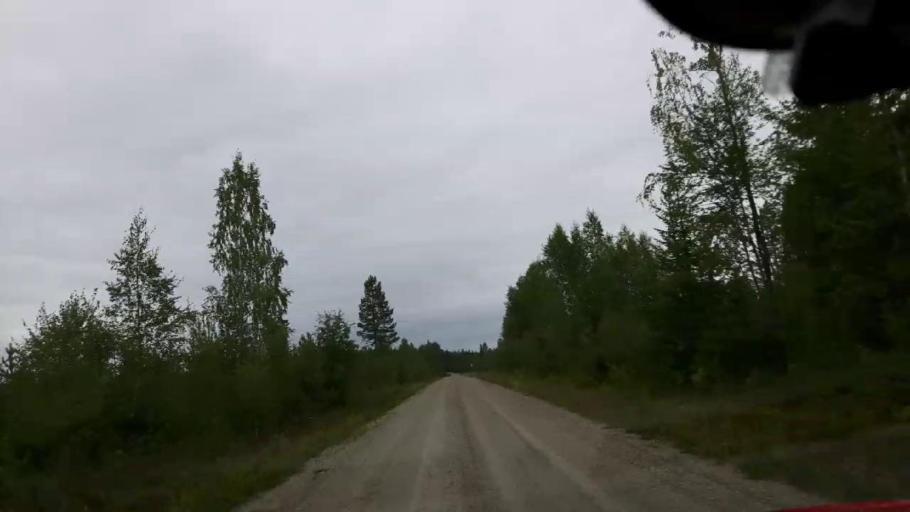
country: SE
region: Vaesternorrland
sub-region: Ange Kommun
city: Ange
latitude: 62.8071
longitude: 15.7428
